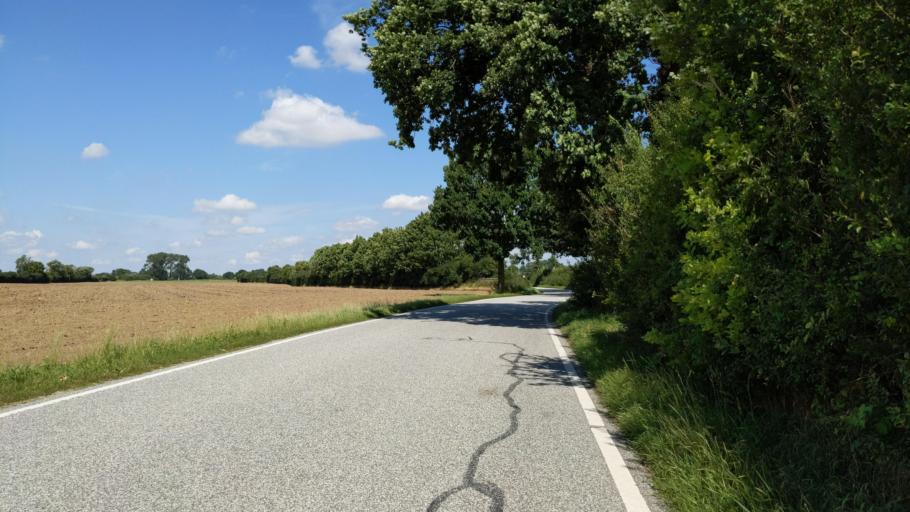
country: DE
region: Schleswig-Holstein
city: Krummesse
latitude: 53.8195
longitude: 10.6728
